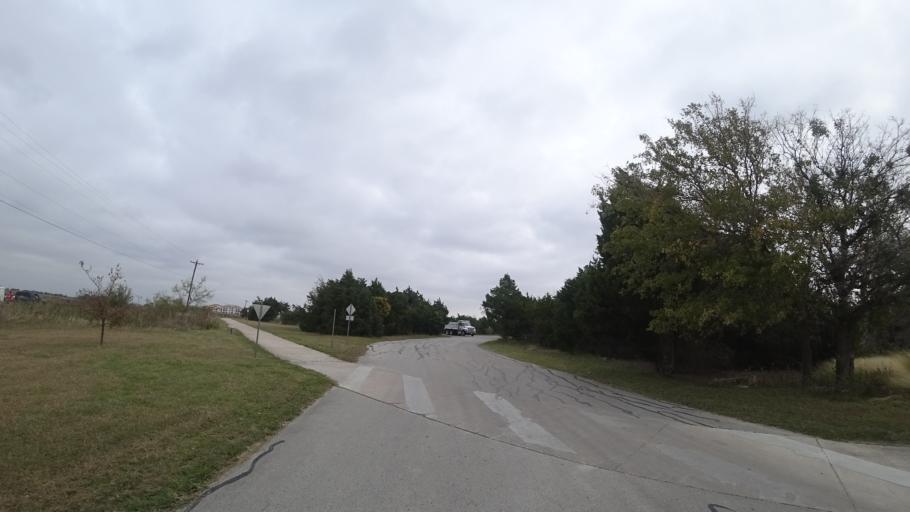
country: US
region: Texas
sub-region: Travis County
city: Pflugerville
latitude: 30.4165
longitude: -97.5964
